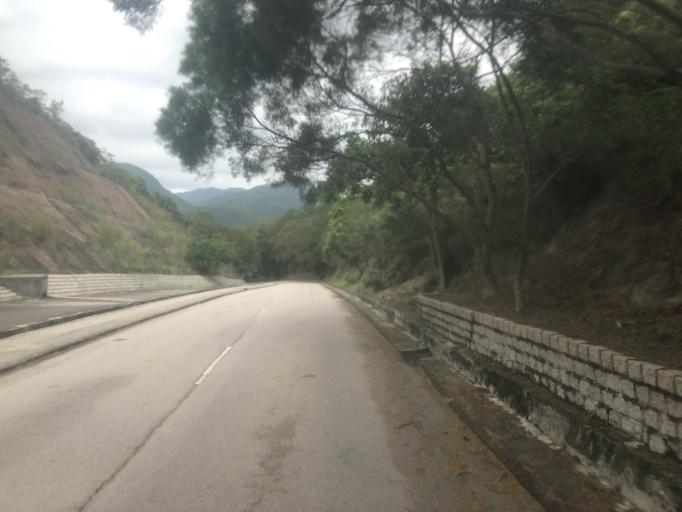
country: HK
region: Sai Kung
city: Sai Kung
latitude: 22.3951
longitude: 114.3300
